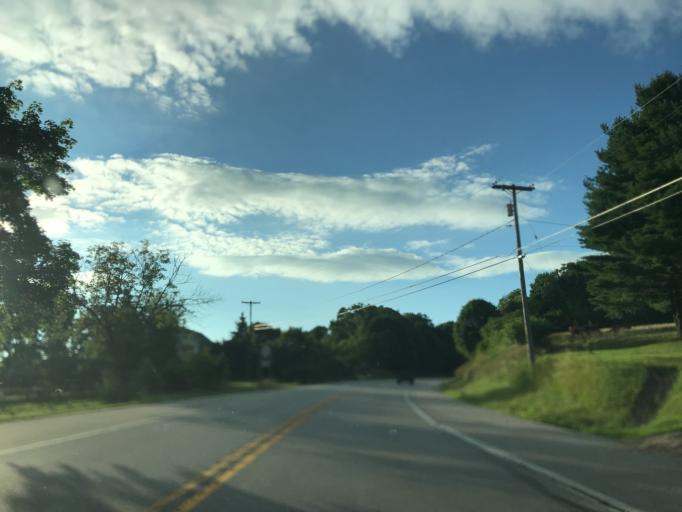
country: US
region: Maryland
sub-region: Carroll County
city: Manchester
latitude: 39.7088
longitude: -76.9166
